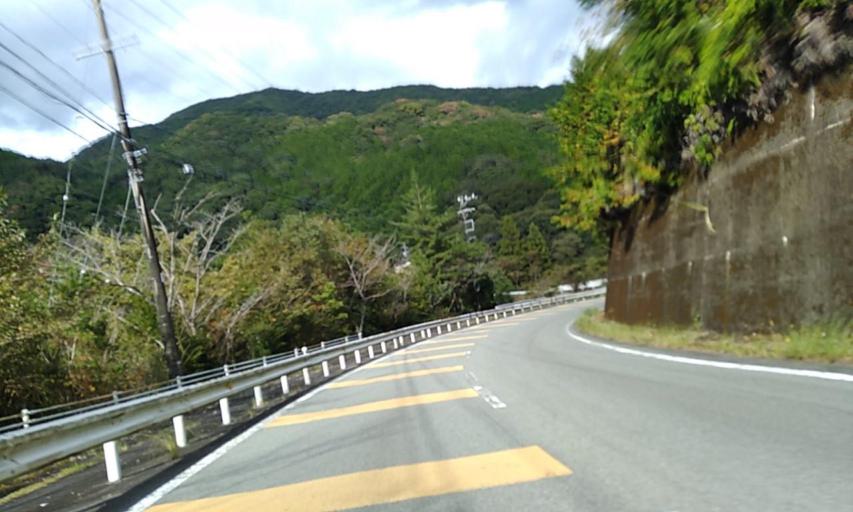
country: JP
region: Mie
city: Ise
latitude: 34.2609
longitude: 136.4820
